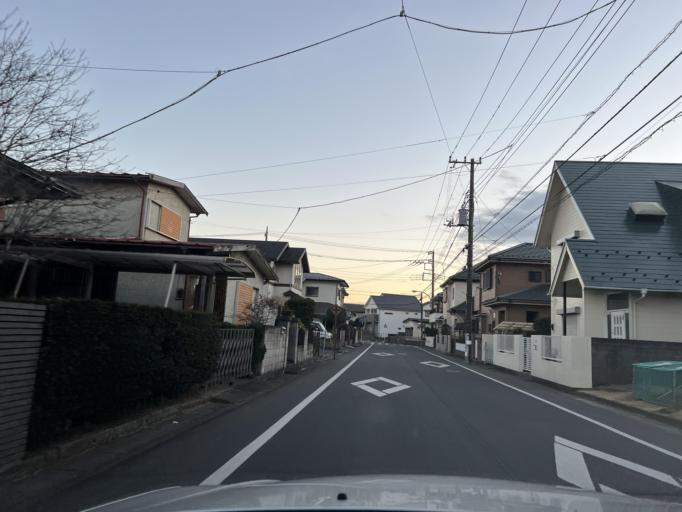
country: JP
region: Chiba
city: Nagareyama
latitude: 35.8845
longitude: 139.9302
